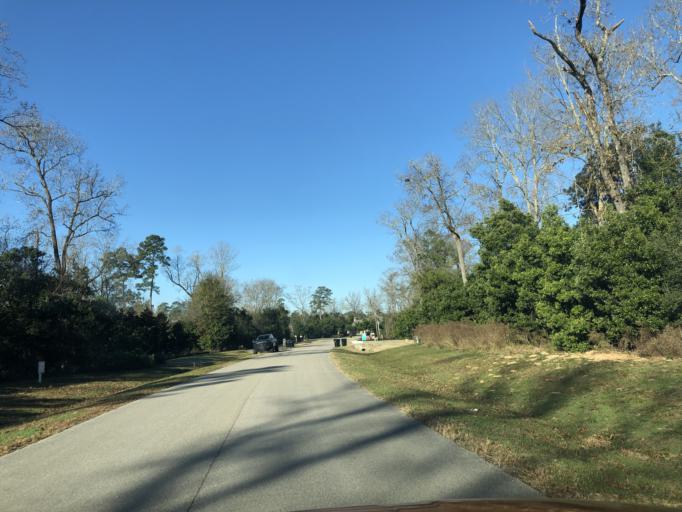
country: US
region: Texas
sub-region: Montgomery County
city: Porter Heights
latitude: 30.0709
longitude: -95.3326
